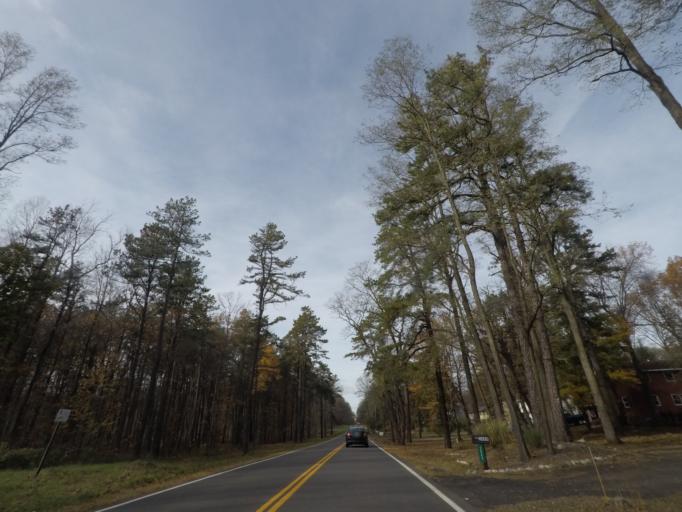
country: US
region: New York
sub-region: Albany County
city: Westmere
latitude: 42.7262
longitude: -73.8948
